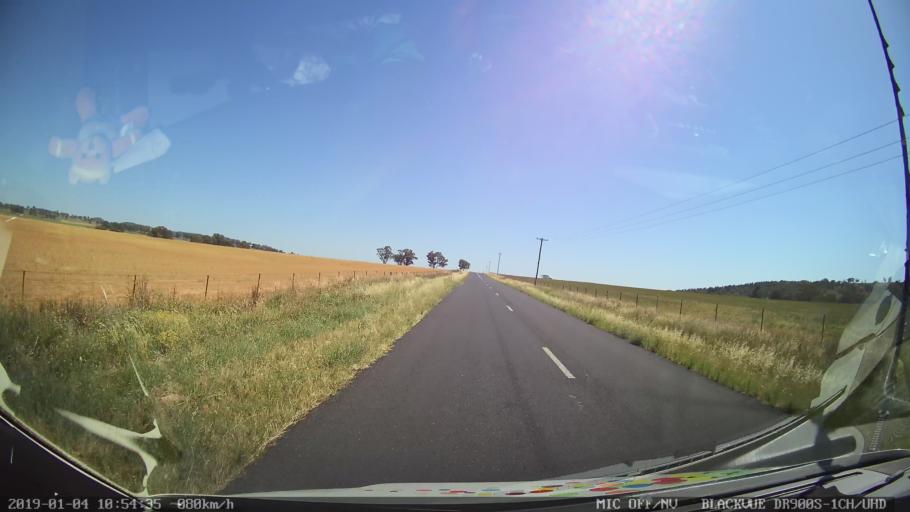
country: AU
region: New South Wales
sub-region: Cabonne
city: Molong
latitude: -33.2033
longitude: 148.6905
